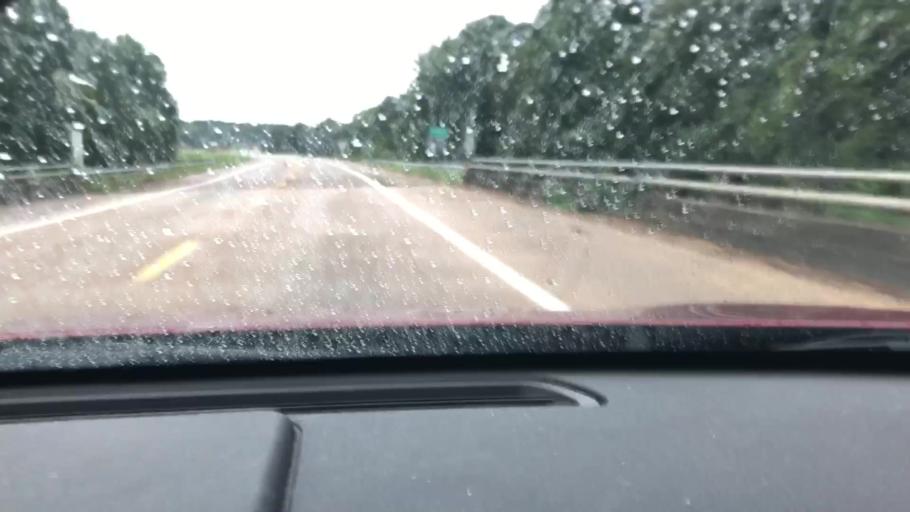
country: US
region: Arkansas
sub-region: Columbia County
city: Magnolia
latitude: 33.2968
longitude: -93.2585
